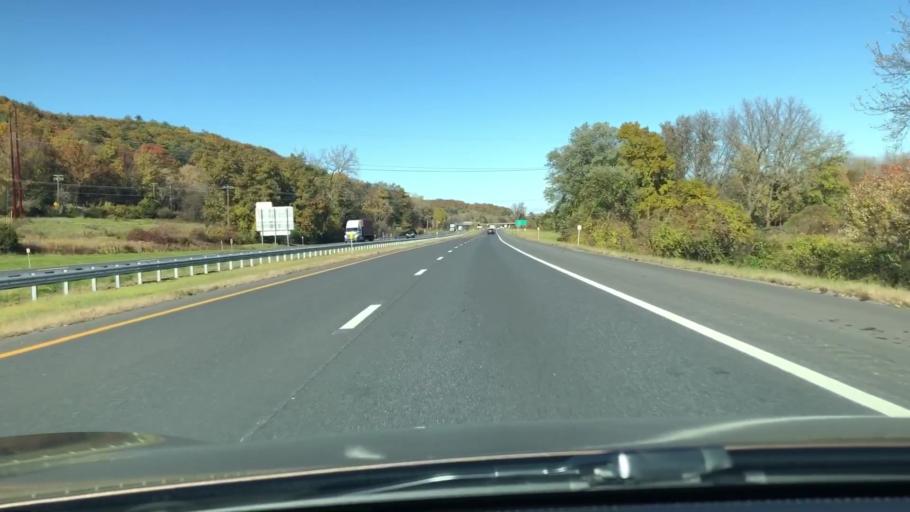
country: US
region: New York
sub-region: Ulster County
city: Lincoln Park
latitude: 41.9651
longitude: -74.0145
